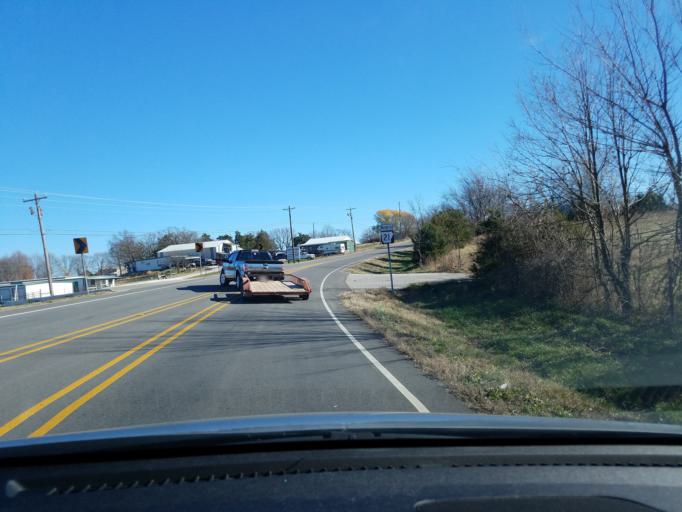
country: US
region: Arkansas
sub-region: Carroll County
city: Berryville
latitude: 36.3922
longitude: -93.5651
